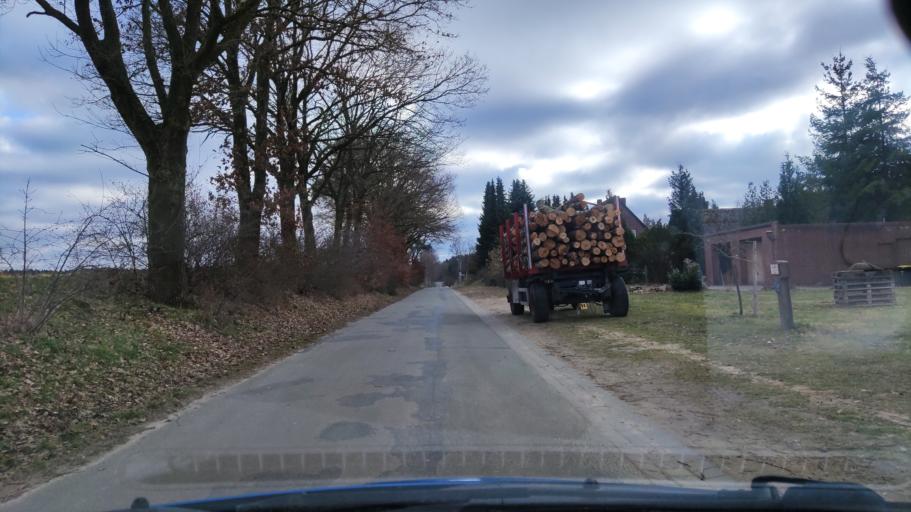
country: DE
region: Lower Saxony
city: Gohrde
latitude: 53.1844
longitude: 10.9455
